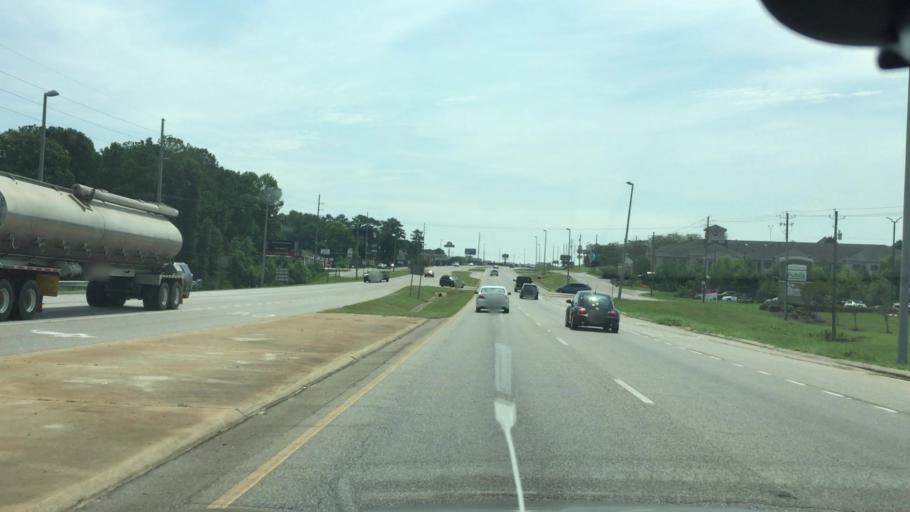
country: US
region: Alabama
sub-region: Coffee County
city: Enterprise
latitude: 31.3284
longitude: -85.8379
